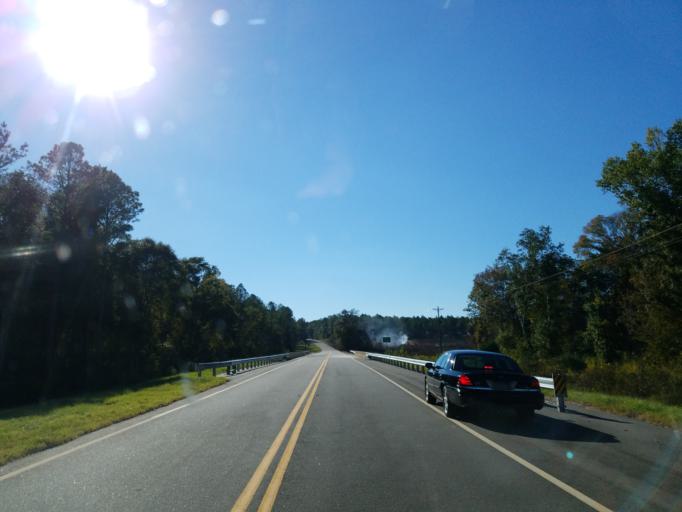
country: US
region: Georgia
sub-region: Dooly County
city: Unadilla
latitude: 32.2446
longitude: -83.8364
